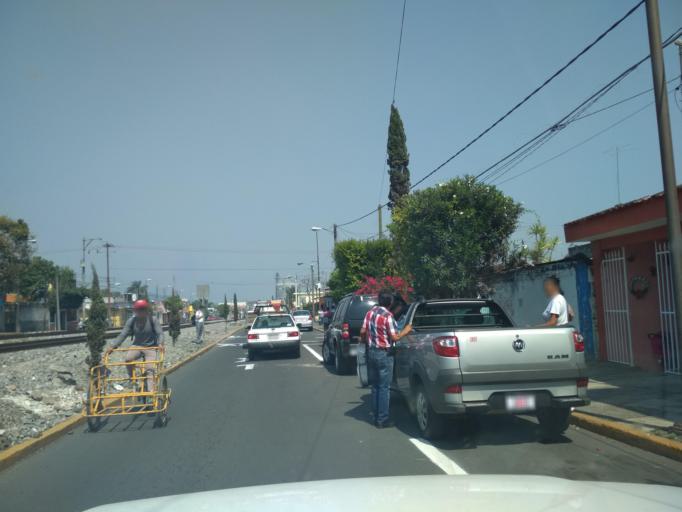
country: MX
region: Veracruz
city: Orizaba
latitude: 18.8443
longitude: -97.0937
